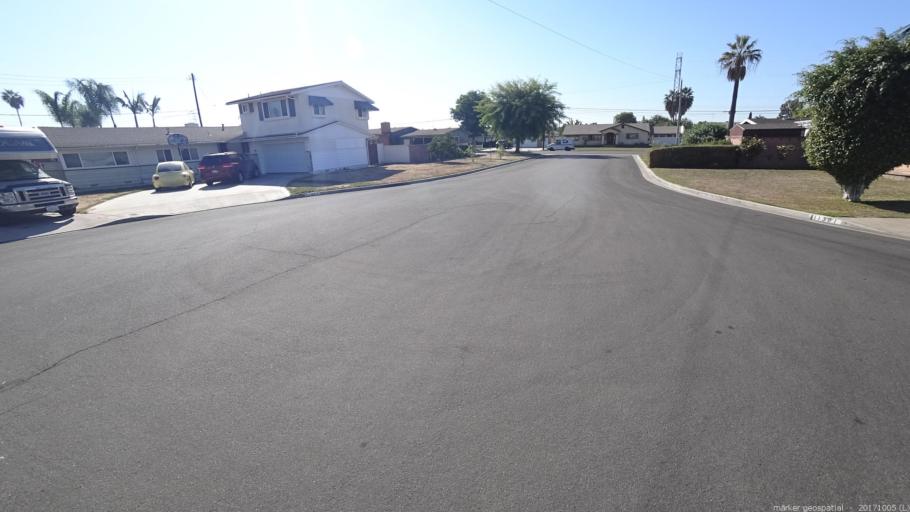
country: US
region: California
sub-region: Orange County
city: Garden Grove
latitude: 33.7987
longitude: -117.9562
